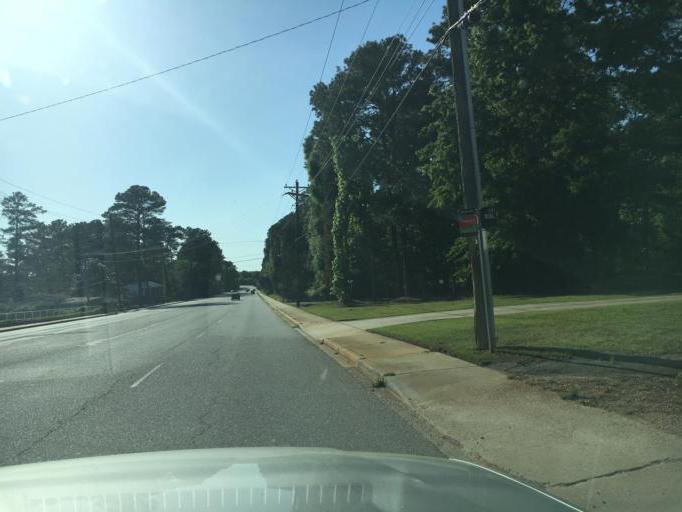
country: US
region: South Carolina
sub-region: Lexington County
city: Seven Oaks
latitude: 34.0444
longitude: -81.1421
